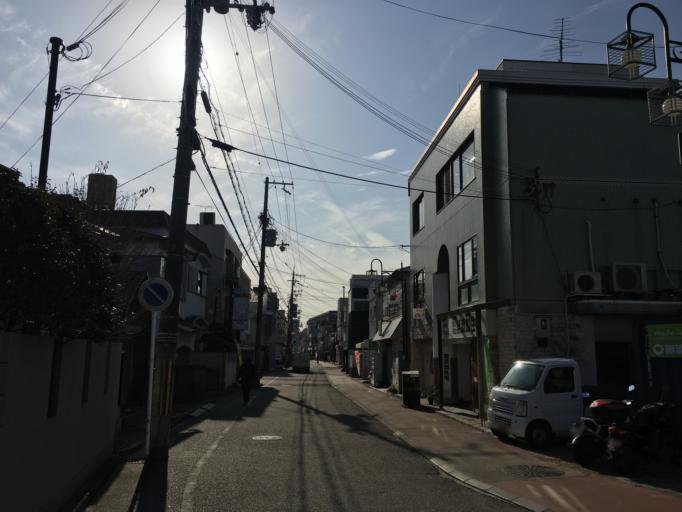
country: JP
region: Hyogo
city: Takarazuka
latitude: 34.7594
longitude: 135.3604
